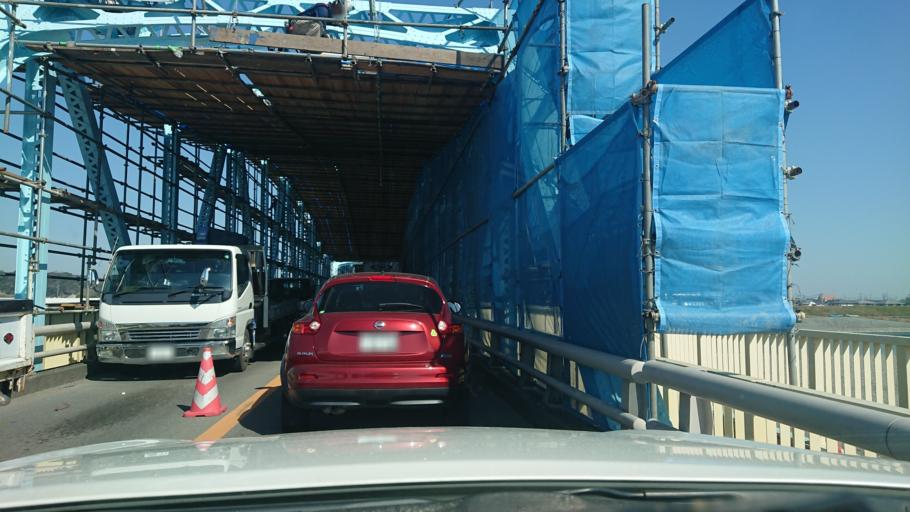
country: JP
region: Tokushima
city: Anan
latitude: 33.9387
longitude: 134.6218
